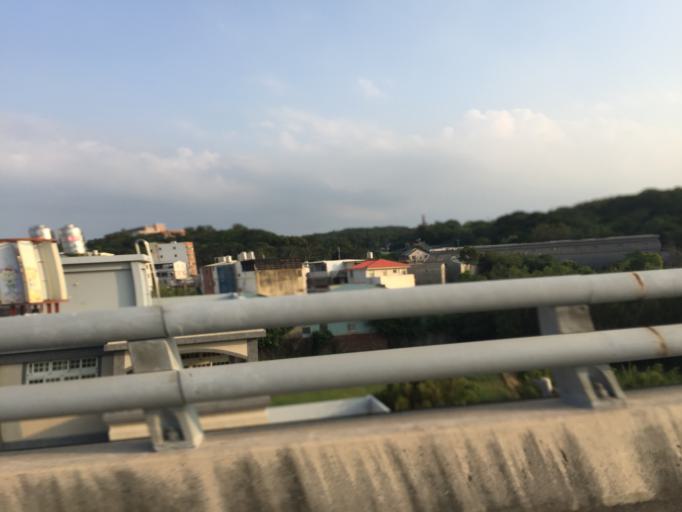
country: TW
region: Taiwan
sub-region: Hsinchu
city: Hsinchu
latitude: 24.7937
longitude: 120.9479
